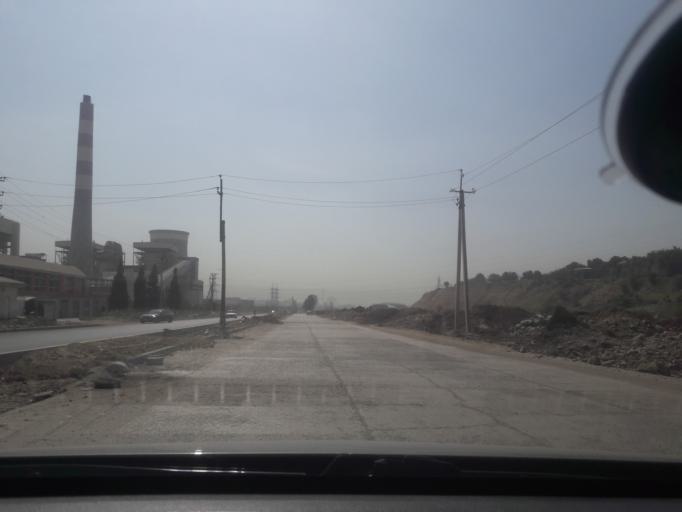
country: TJ
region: Dushanbe
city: Dushanbe
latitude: 38.6134
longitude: 68.7696
